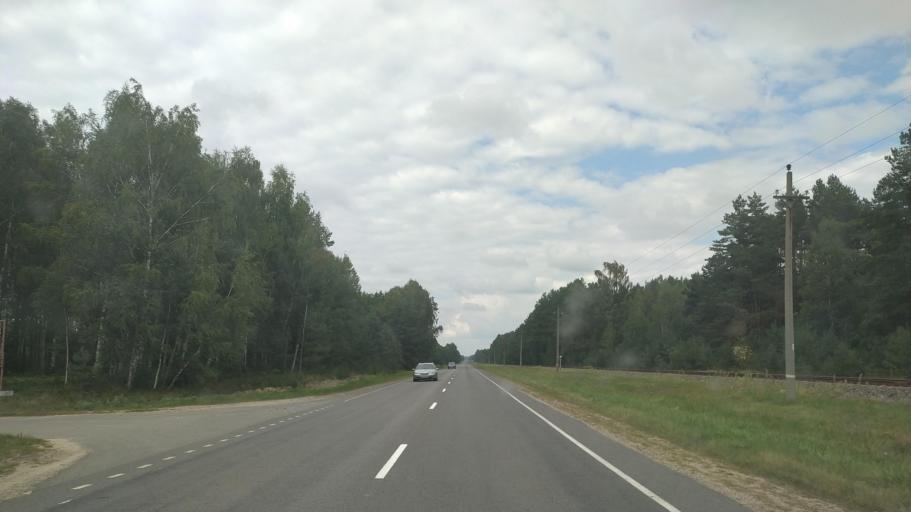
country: BY
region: Brest
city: Byelaazyorsk
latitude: 52.5220
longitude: 25.1497
